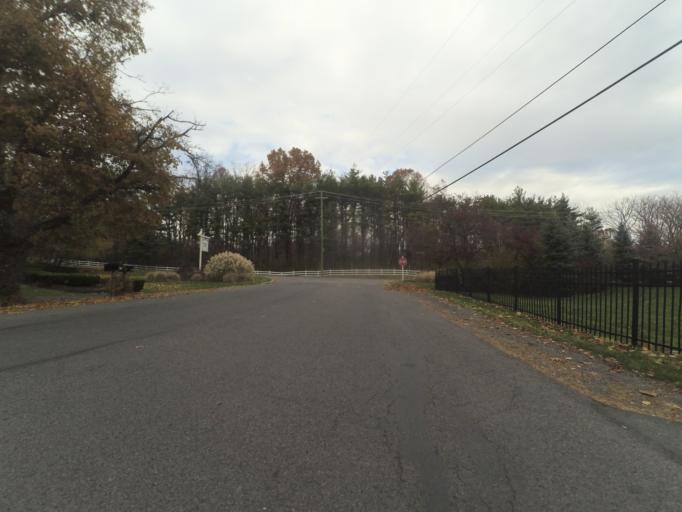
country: US
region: Pennsylvania
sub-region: Centre County
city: Boalsburg
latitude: 40.7824
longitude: -77.8144
